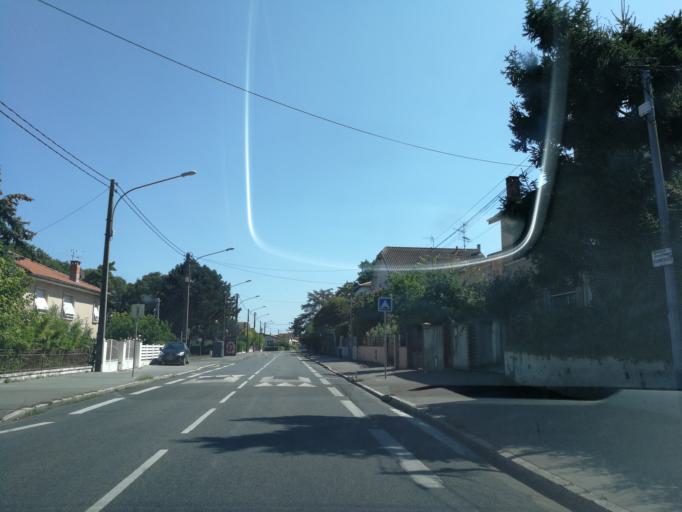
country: FR
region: Midi-Pyrenees
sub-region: Departement de la Haute-Garonne
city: Toulouse
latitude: 43.6239
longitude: 1.4667
